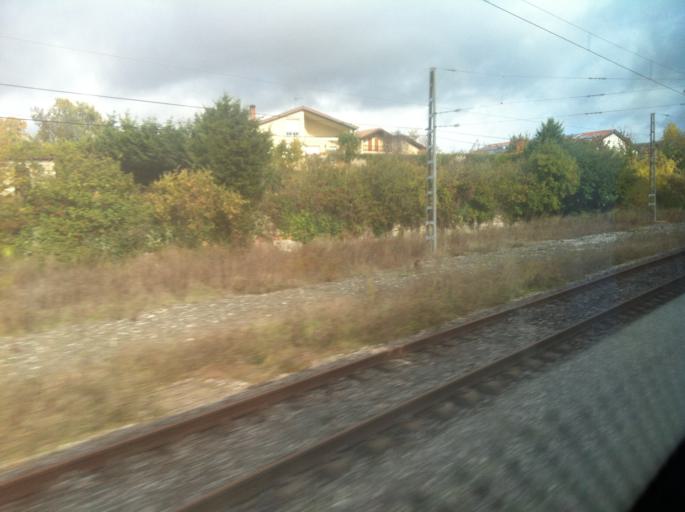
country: ES
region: Basque Country
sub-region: Provincia de Alava
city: Arminon
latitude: 42.7437
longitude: -2.8663
